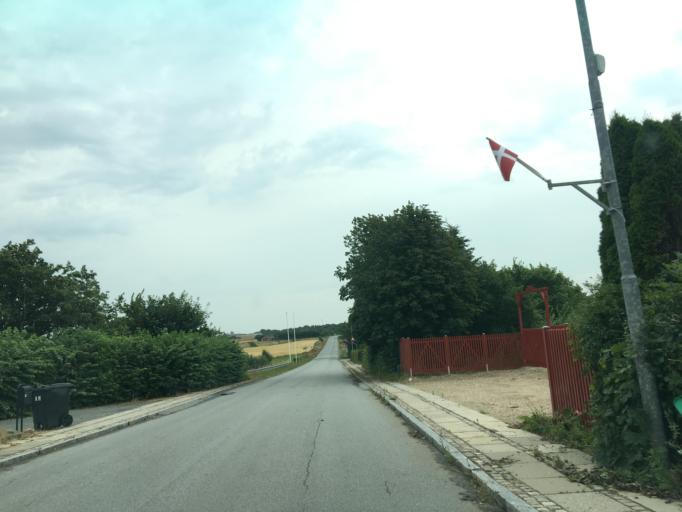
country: DK
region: North Denmark
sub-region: Thisted Kommune
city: Hurup
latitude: 56.8047
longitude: 8.4077
